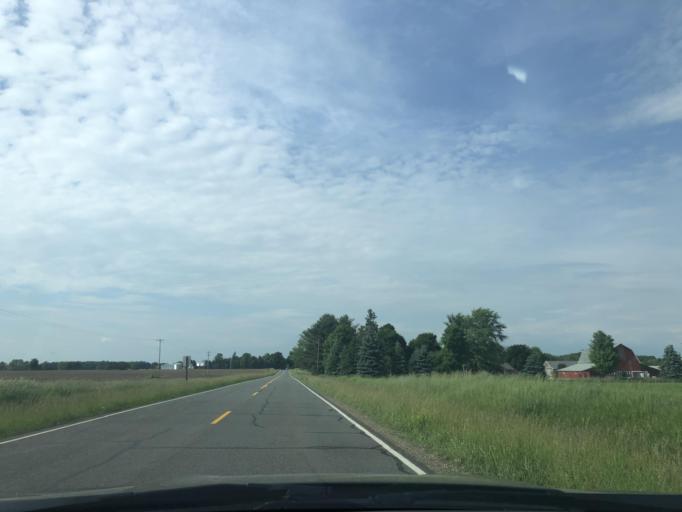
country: US
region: Michigan
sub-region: Clinton County
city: Bath
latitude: 42.8298
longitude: -84.4838
